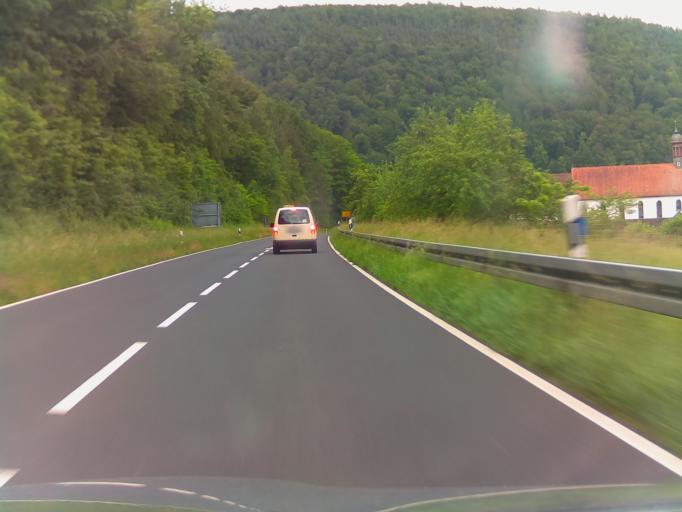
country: DE
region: Bavaria
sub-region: Regierungsbezirk Unterfranken
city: Schonau
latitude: 50.0789
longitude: 9.7203
